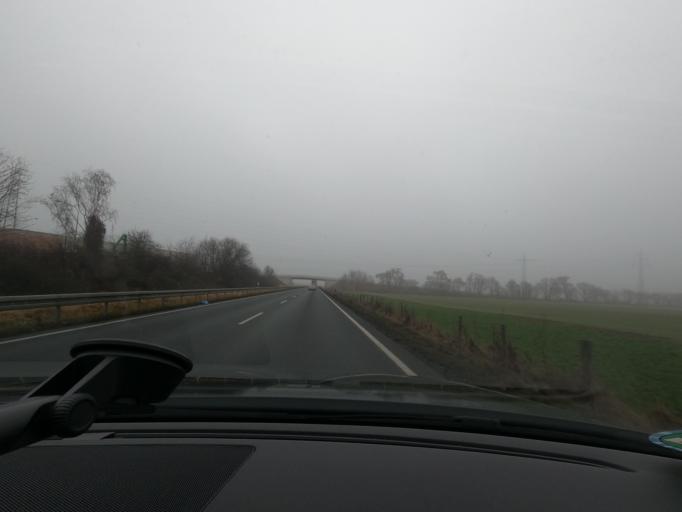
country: DE
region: North Rhine-Westphalia
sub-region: Regierungsbezirk Koln
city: Dueren
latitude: 50.7838
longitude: 6.5166
